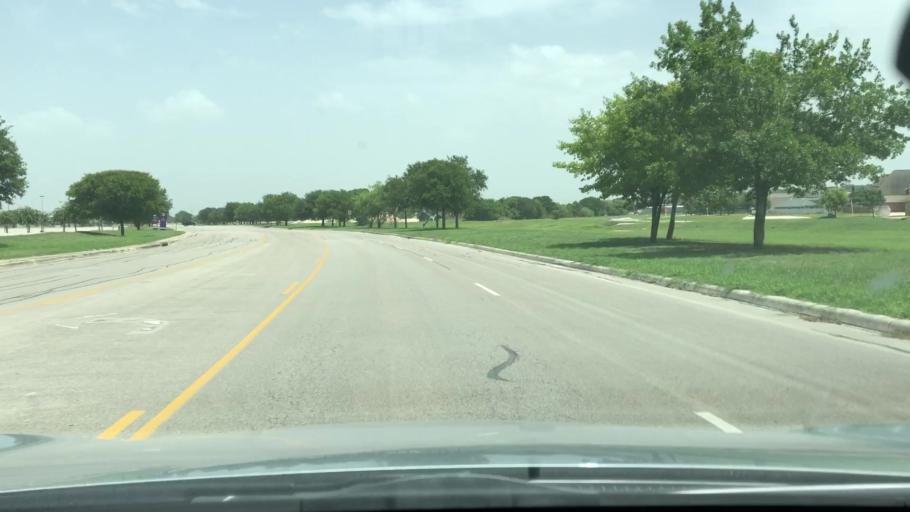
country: US
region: Texas
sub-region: Bexar County
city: Selma
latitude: 29.5839
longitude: -98.3220
